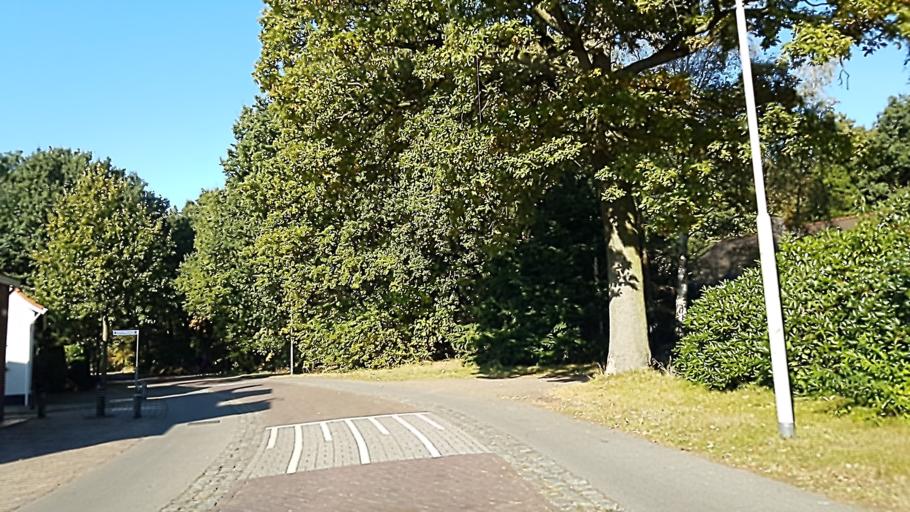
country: NL
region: North Brabant
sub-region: Gemeente Woensdrecht
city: Woensdrecht
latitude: 51.4388
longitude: 4.3182
